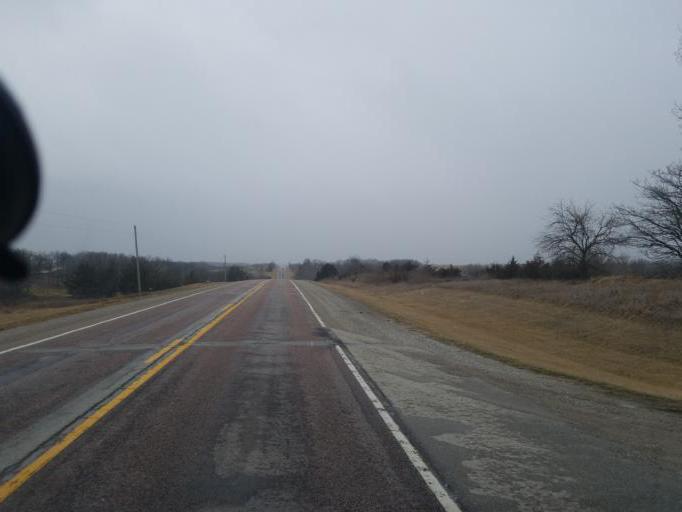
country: US
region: Iowa
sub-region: Appanoose County
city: Centerville
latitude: 40.6276
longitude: -92.9450
